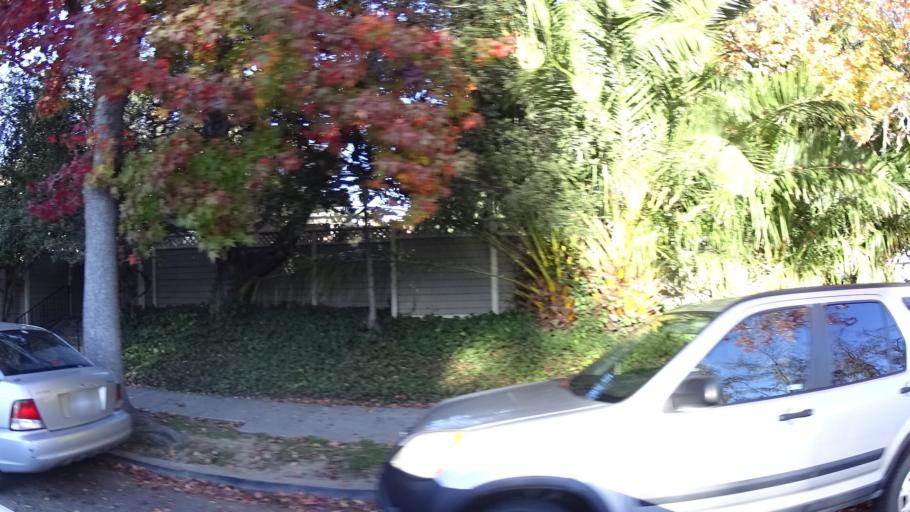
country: US
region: California
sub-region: Alameda County
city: Piedmont
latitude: 37.8080
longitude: -122.2222
